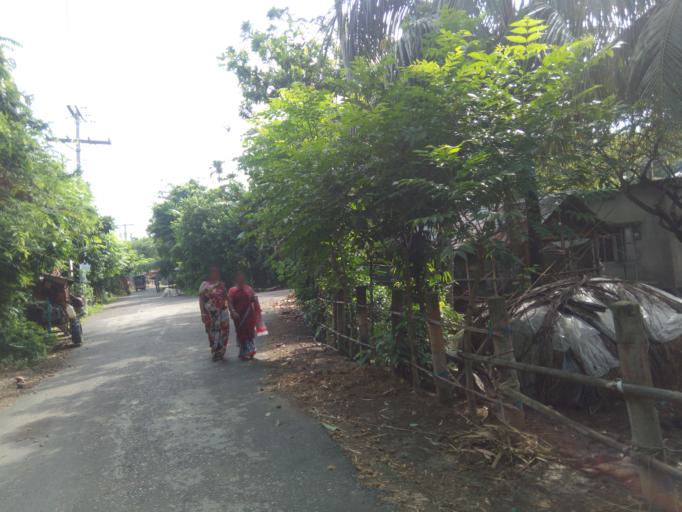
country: BD
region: Khulna
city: Kalia
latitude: 22.9596
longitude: 89.5552
